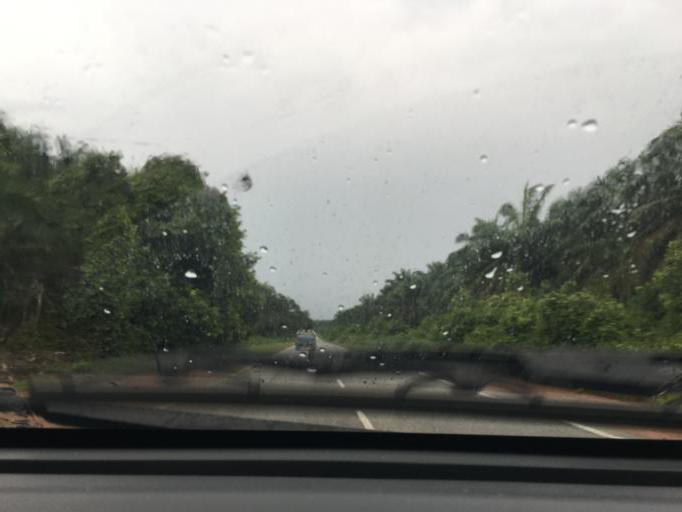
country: MY
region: Kedah
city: Sungai Petani
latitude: 5.6363
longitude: 100.6293
